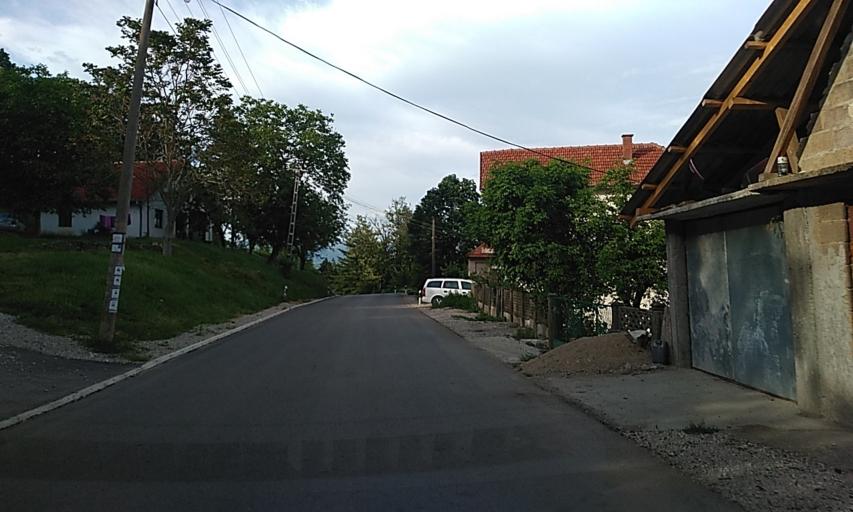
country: RS
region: Central Serbia
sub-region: Nisavski Okrug
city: Aleksinac
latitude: 43.4163
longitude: 21.7454
